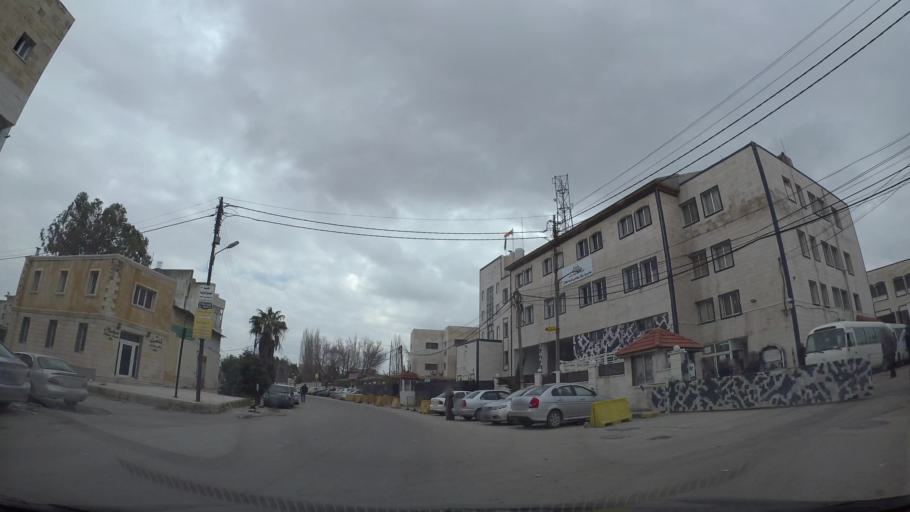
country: JO
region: Amman
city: Wadi as Sir
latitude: 31.9463
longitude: 35.8315
